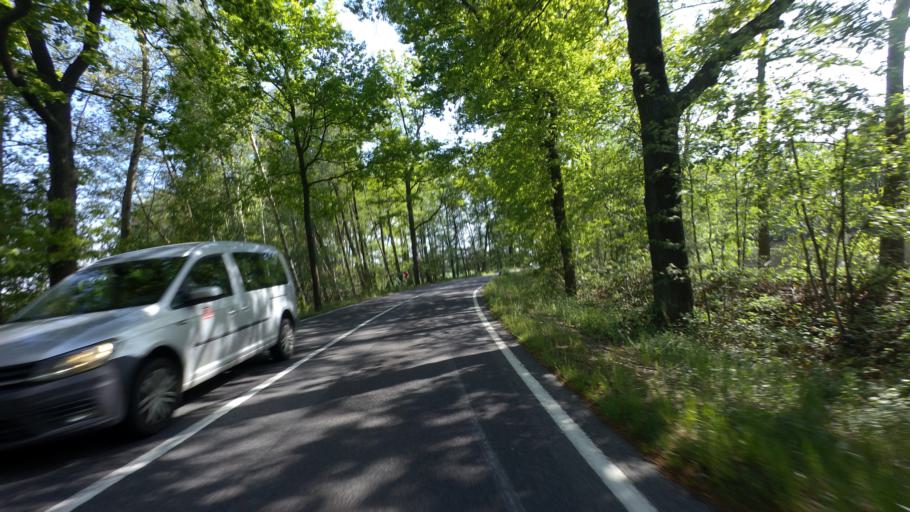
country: DE
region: Saxony
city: Ossling
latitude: 51.3348
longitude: 14.1580
